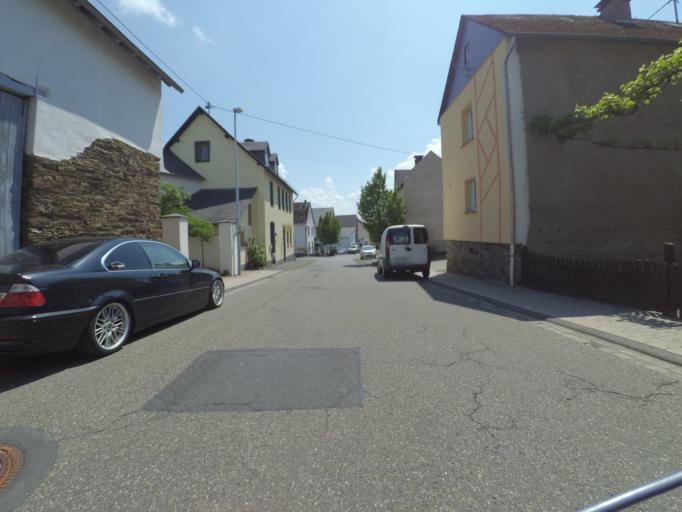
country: DE
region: Rheinland-Pfalz
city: Hambuch
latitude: 50.2262
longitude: 7.1815
